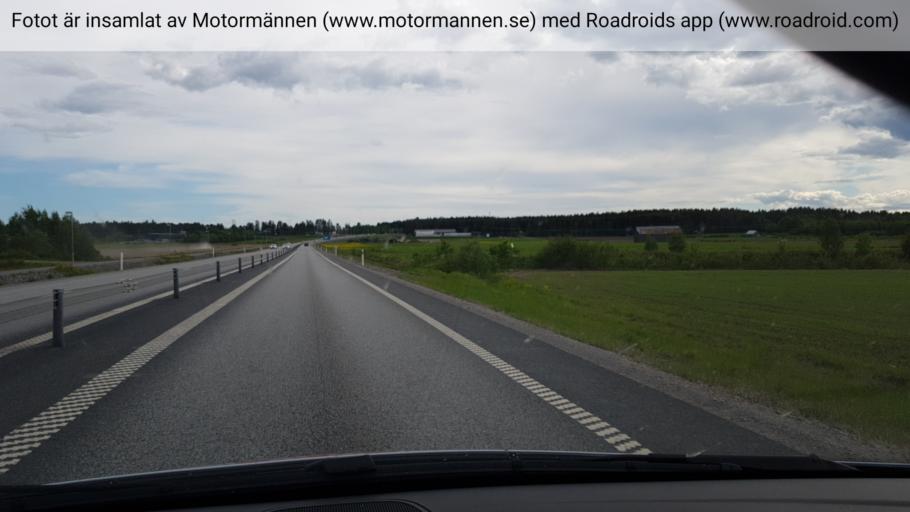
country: SE
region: Vaesterbotten
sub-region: Umea Kommun
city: Roback
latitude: 63.8502
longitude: 20.1909
